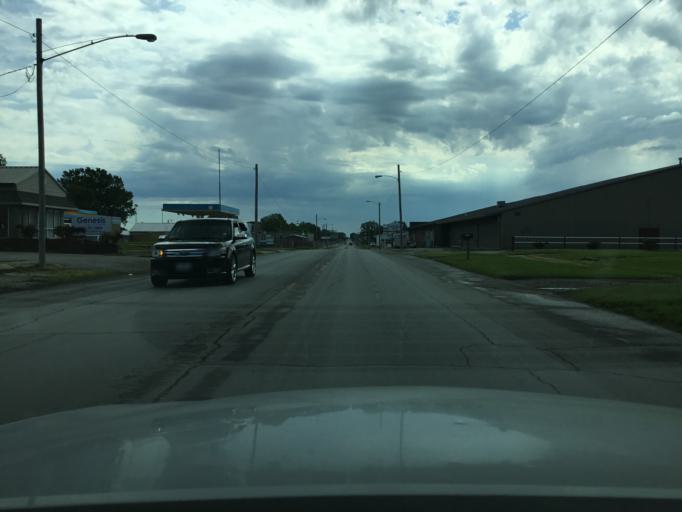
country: US
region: Kansas
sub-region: Montgomery County
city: Coffeyville
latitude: 37.0362
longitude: -95.6377
